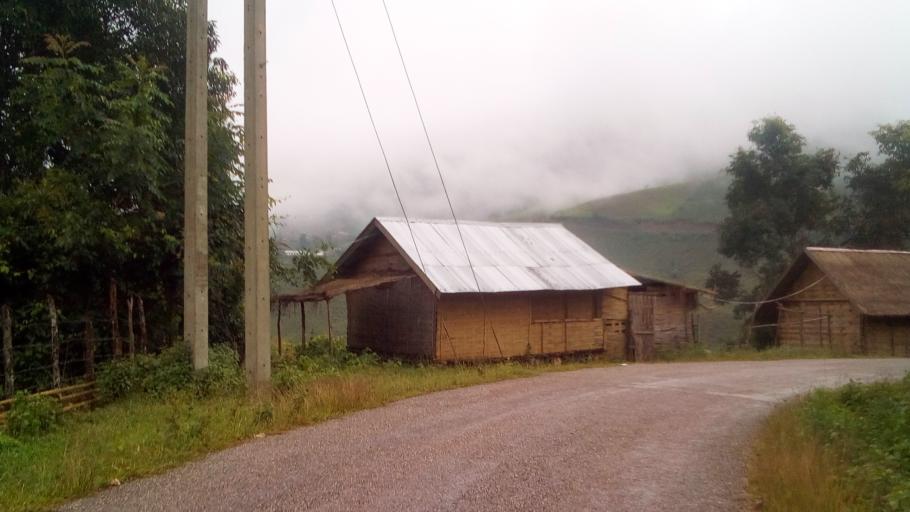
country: TH
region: Nan
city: Chaloem Phra Kiat
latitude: 19.4337
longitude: 101.2397
